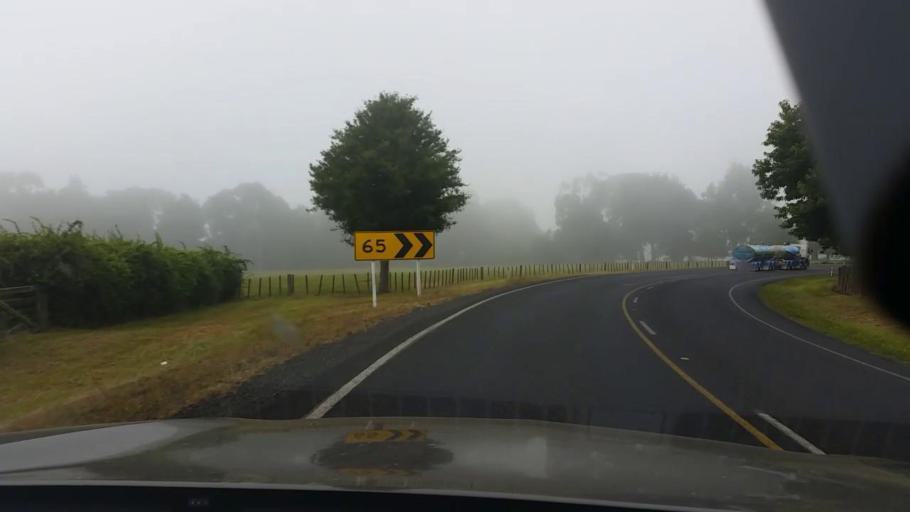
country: NZ
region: Waikato
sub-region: Hamilton City
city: Hamilton
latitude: -37.6509
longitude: 175.2982
